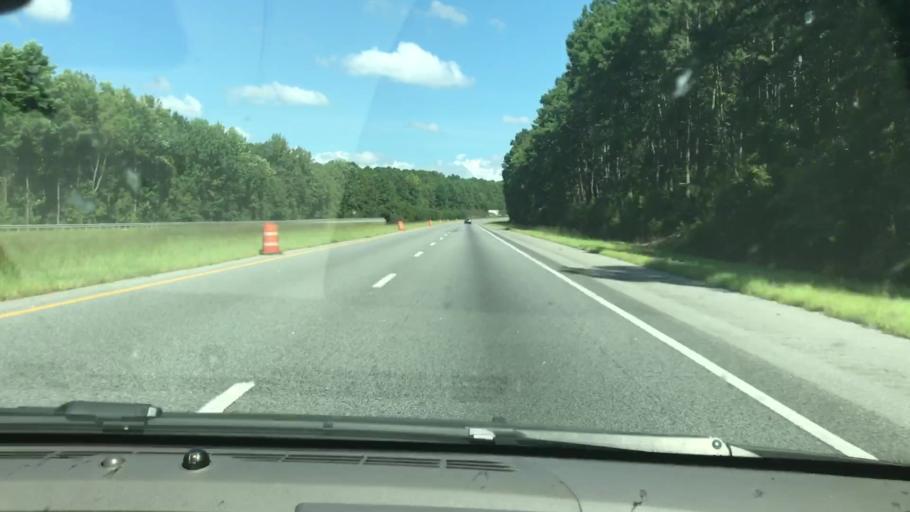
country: US
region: Georgia
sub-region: Harris County
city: Hamilton
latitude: 32.7154
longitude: -85.0162
